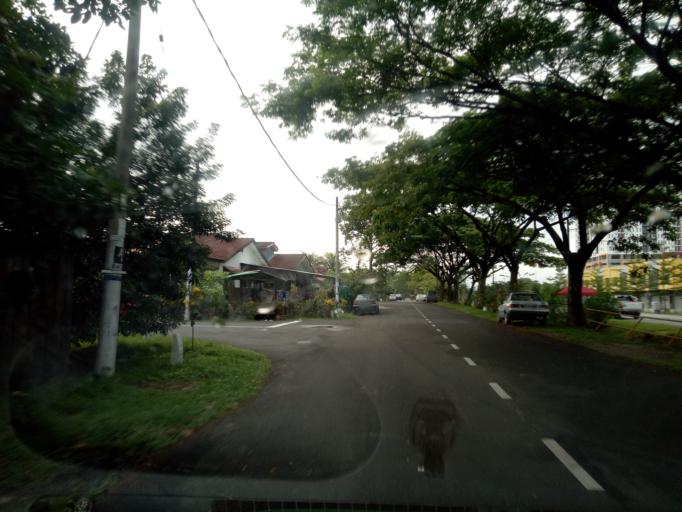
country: MY
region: Selangor
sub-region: Hulu Langat
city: Semenyih
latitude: 2.9276
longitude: 101.8602
